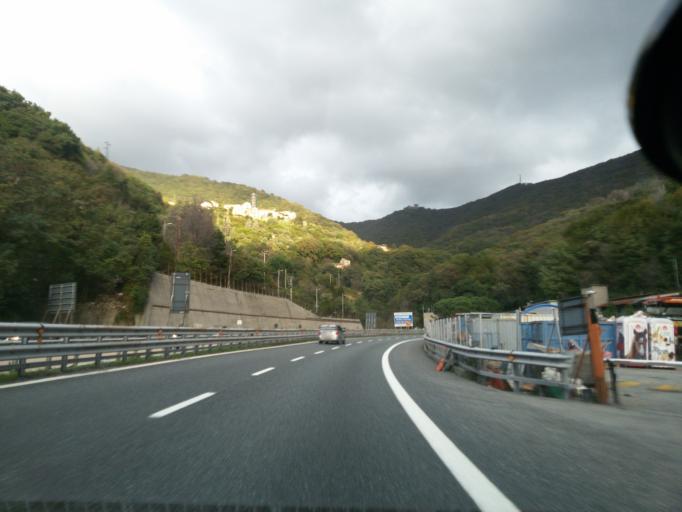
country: IT
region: Liguria
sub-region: Provincia di Genova
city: Genoa
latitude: 44.4460
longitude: 8.9180
